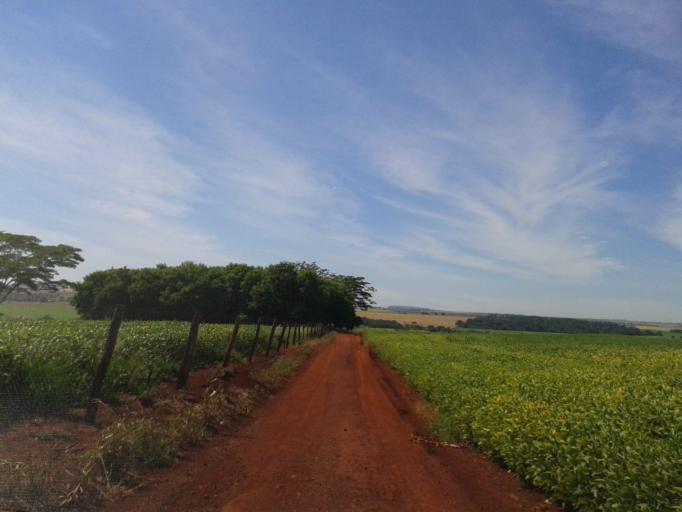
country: BR
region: Minas Gerais
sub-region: Capinopolis
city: Capinopolis
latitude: -18.6415
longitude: -49.7165
